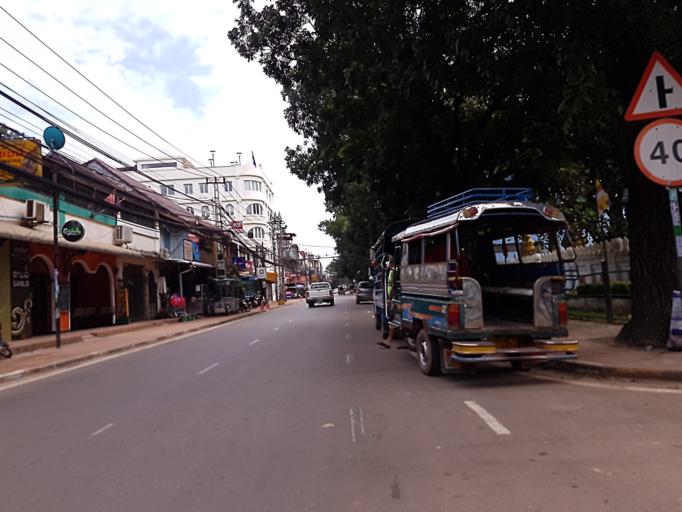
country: LA
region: Vientiane
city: Vientiane
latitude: 17.9660
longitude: 102.6043
